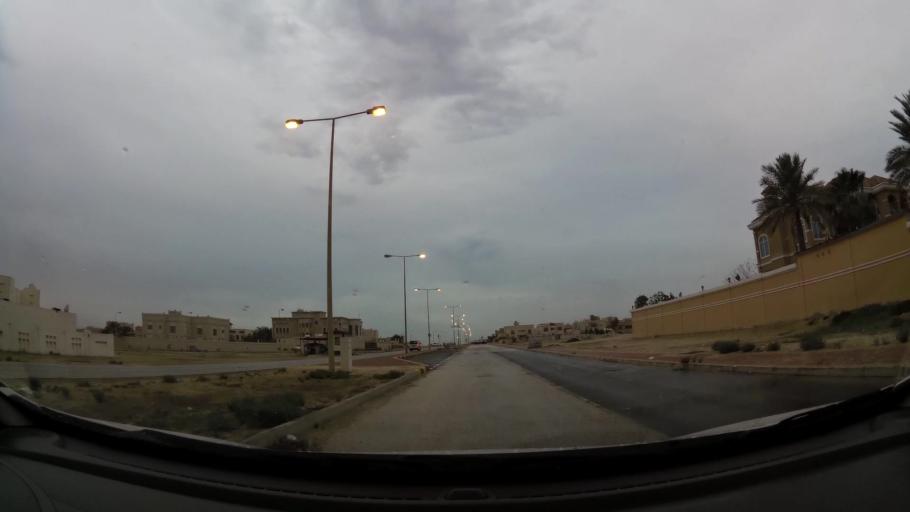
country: BH
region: Central Governorate
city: Madinat Hamad
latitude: 26.1437
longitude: 50.5171
